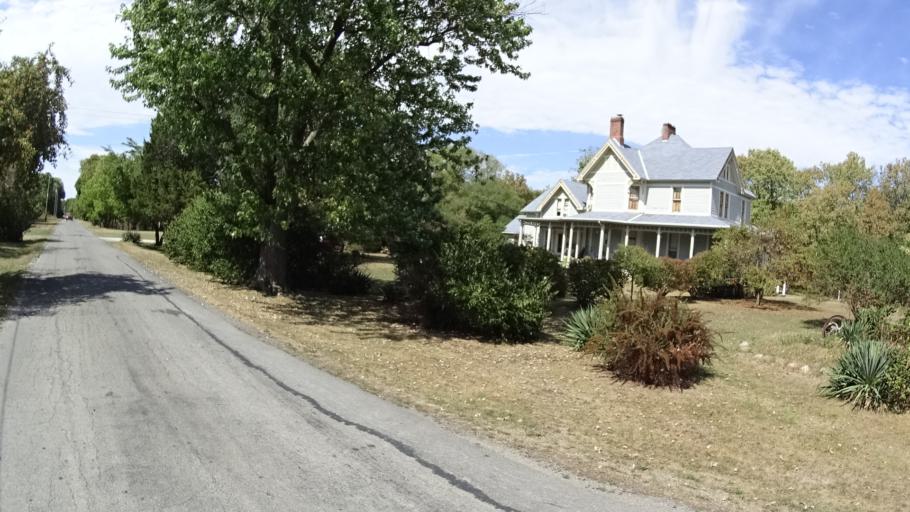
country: US
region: Ohio
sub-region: Erie County
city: Sandusky
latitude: 41.6053
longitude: -82.7088
